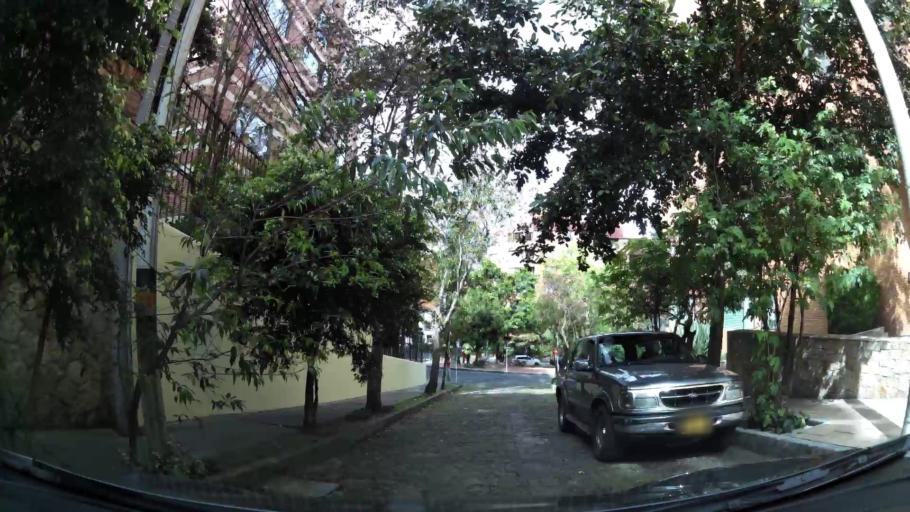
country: CO
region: Bogota D.C.
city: Barrio San Luis
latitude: 4.6567
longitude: -74.0506
